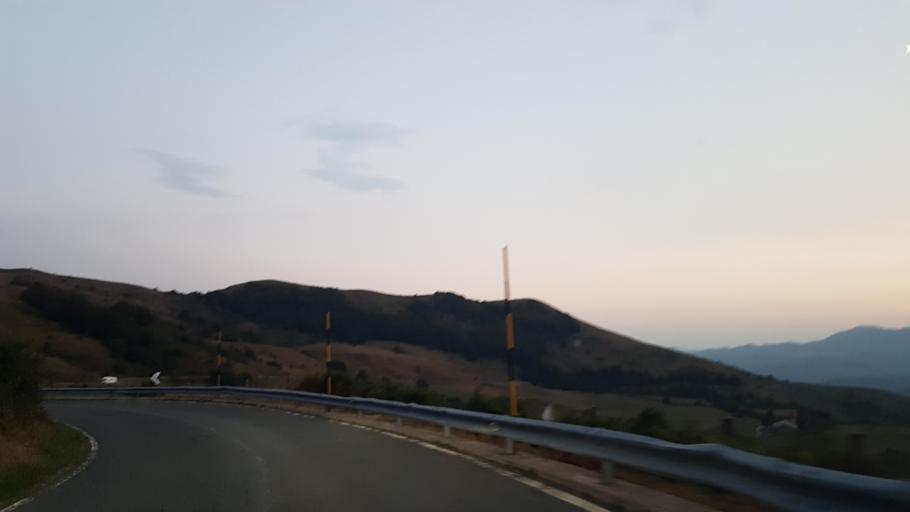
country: IT
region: Liguria
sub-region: Provincia di La Spezia
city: Varese Ligure
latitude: 44.4165
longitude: 9.6285
